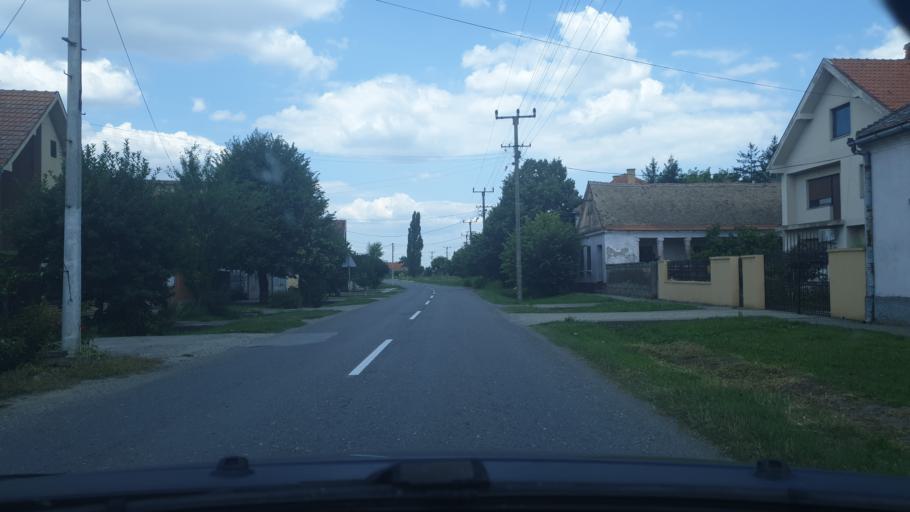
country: RS
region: Autonomna Pokrajina Vojvodina
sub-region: Sremski Okrug
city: Pecinci
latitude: 44.8455
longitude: 19.9610
